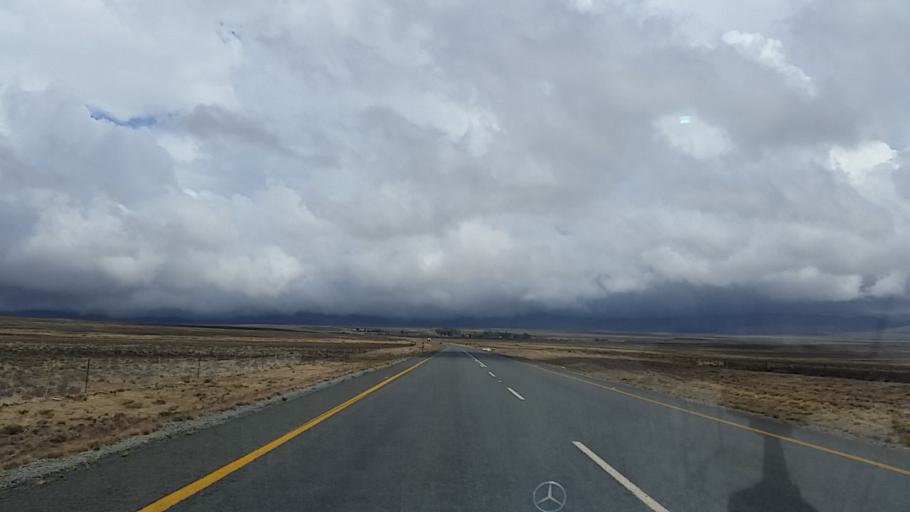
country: ZA
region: Eastern Cape
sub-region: Chris Hani District Municipality
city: Middelburg
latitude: -31.8886
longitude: 24.8012
